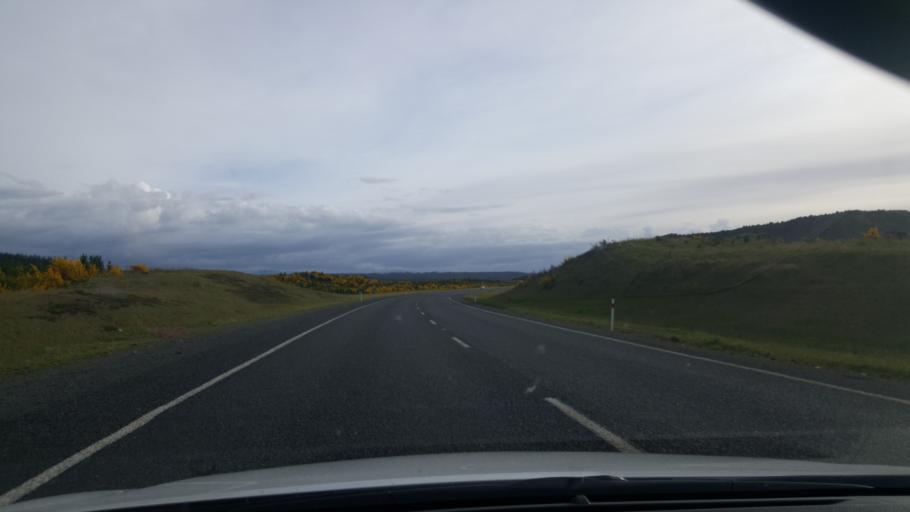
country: NZ
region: Waikato
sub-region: Taupo District
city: Taupo
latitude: -38.8379
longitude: 176.0644
